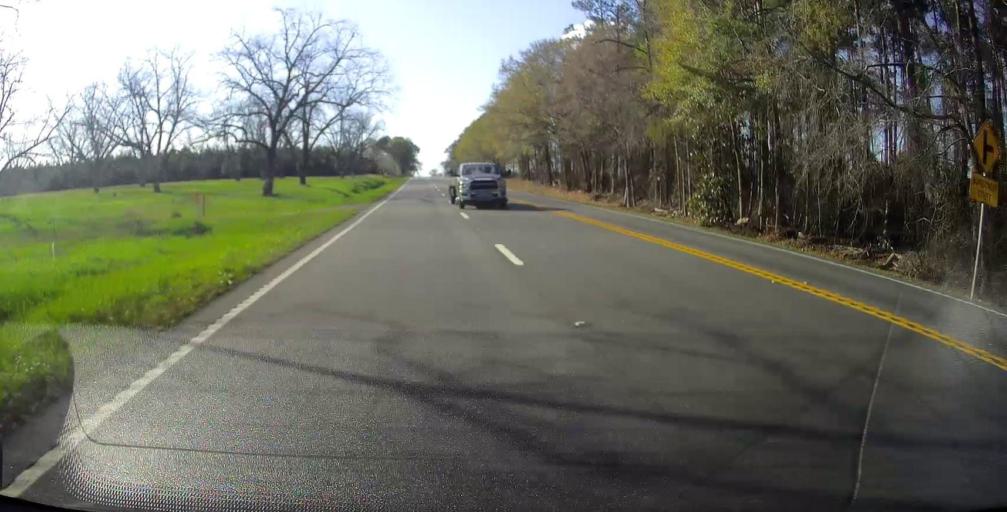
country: US
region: Georgia
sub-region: Montgomery County
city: Mount Vernon
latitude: 32.1815
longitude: -82.5594
